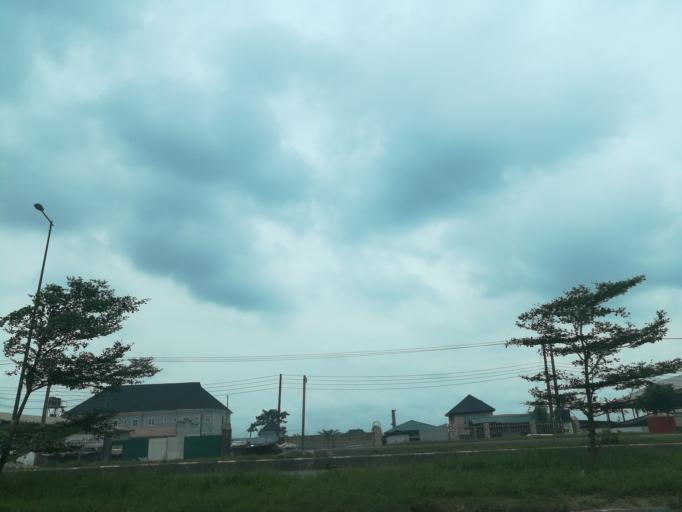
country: NG
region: Lagos
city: Ojota
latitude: 6.6120
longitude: 3.4178
